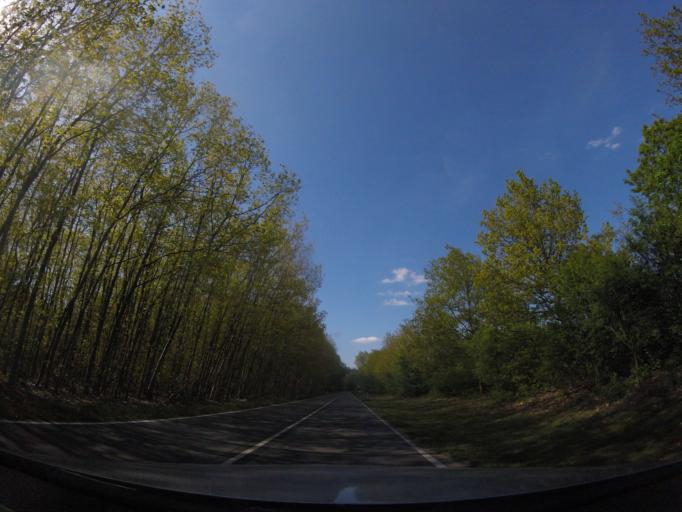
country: DE
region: Hesse
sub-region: Regierungsbezirk Darmstadt
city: Buttelborn
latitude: 49.9411
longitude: 8.5445
